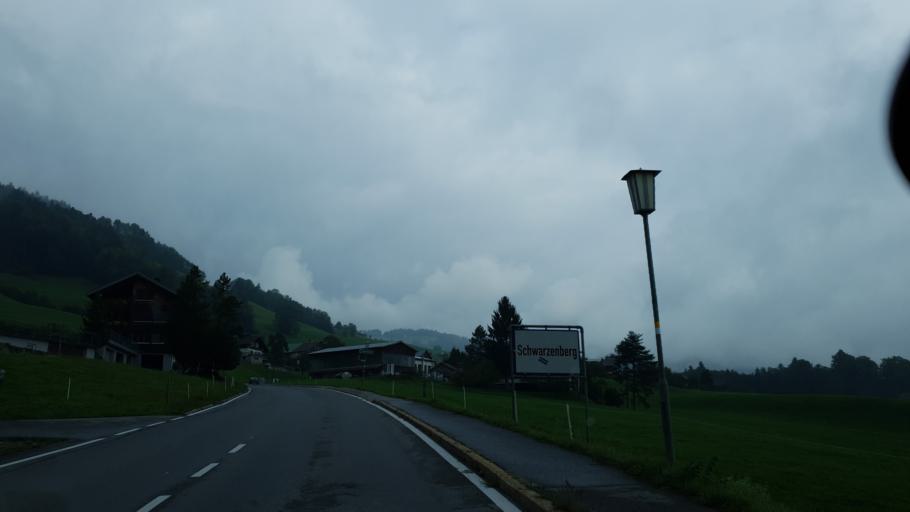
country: AT
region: Vorarlberg
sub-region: Politischer Bezirk Bregenz
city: Andelsbuch
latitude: 47.4023
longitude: 9.8512
